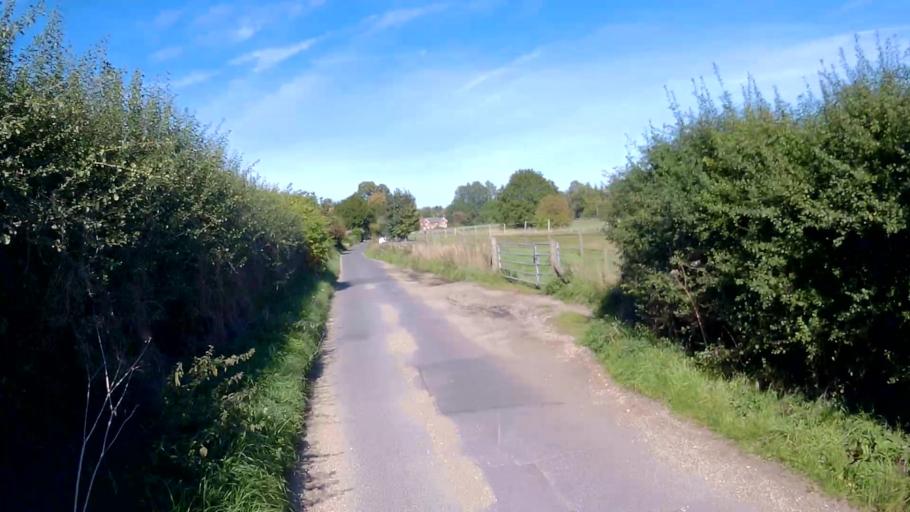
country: GB
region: England
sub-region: Hampshire
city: Andover
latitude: 51.1502
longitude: -1.4628
